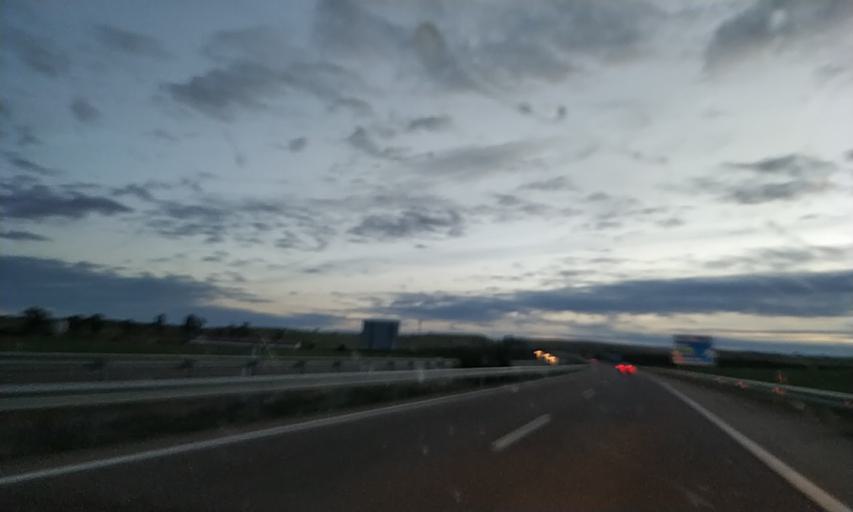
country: ES
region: Extremadura
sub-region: Provincia de Badajoz
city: Badajoz
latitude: 38.9165
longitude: -6.9820
